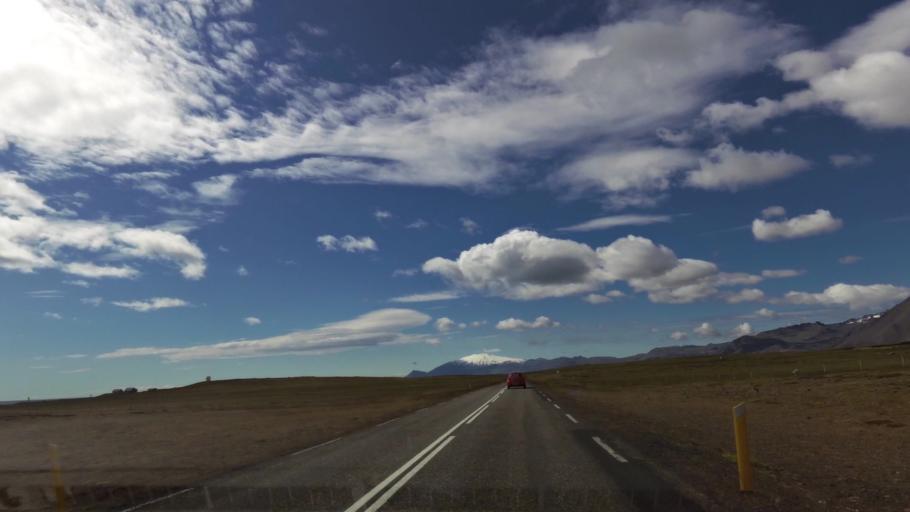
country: IS
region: West
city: Stykkisholmur
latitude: 64.8089
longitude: -23.0823
